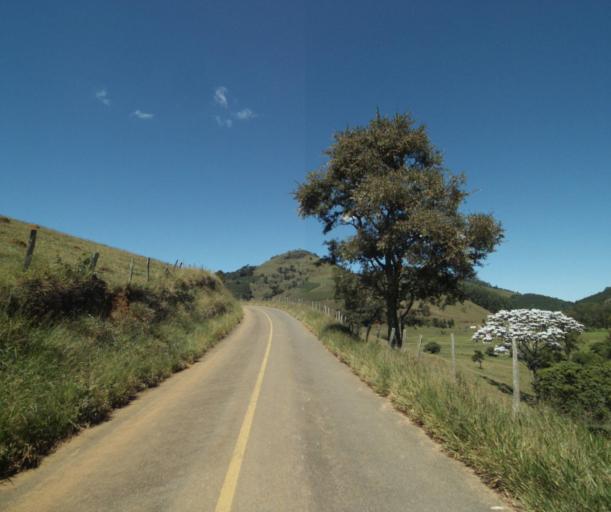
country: BR
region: Minas Gerais
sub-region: Espera Feliz
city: Espera Feliz
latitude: -20.6230
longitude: -41.8353
